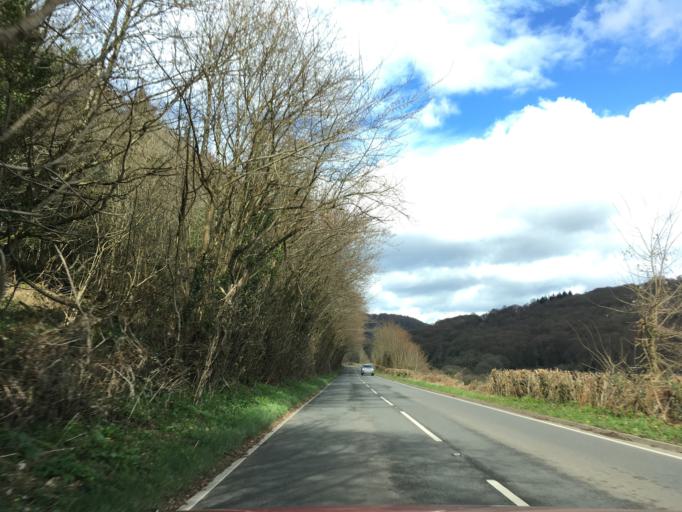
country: GB
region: Wales
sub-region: Monmouthshire
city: Tintern
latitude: 51.7214
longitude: -2.6843
